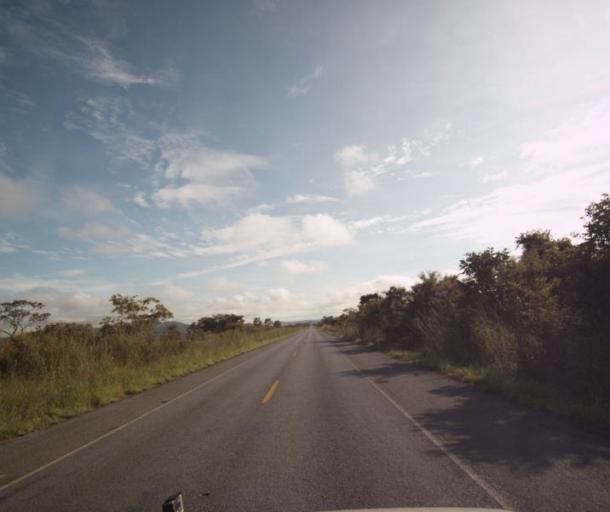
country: BR
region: Goias
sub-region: Pirenopolis
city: Pirenopolis
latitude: -15.5202
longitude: -48.6239
